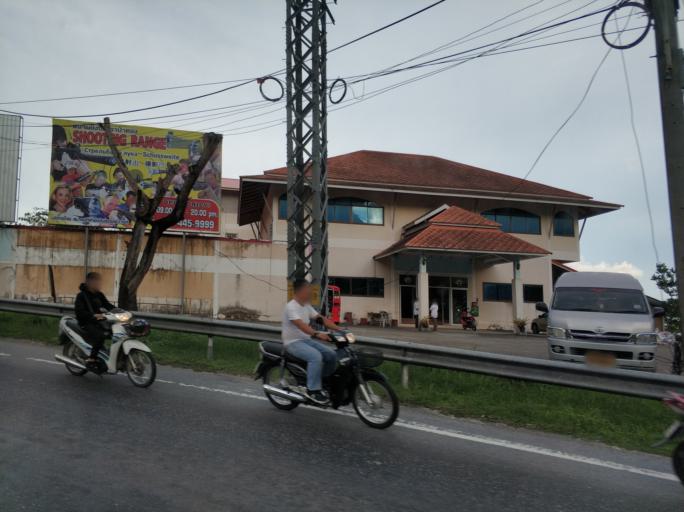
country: TH
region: Phuket
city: Kathu
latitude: 7.9056
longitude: 98.3245
